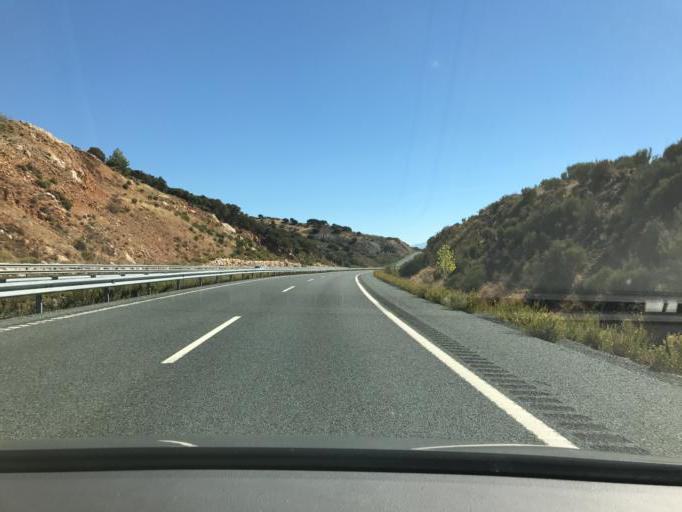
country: ES
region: Andalusia
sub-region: Provincia de Granada
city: Diezma
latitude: 37.3157
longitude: -3.3908
